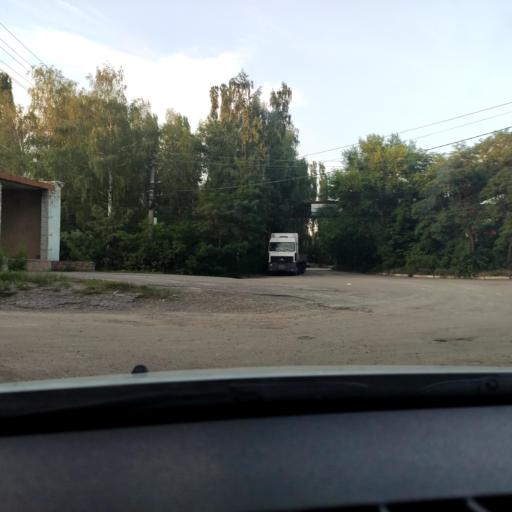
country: RU
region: Voronezj
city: Pridonskoy
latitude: 51.6745
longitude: 39.0857
